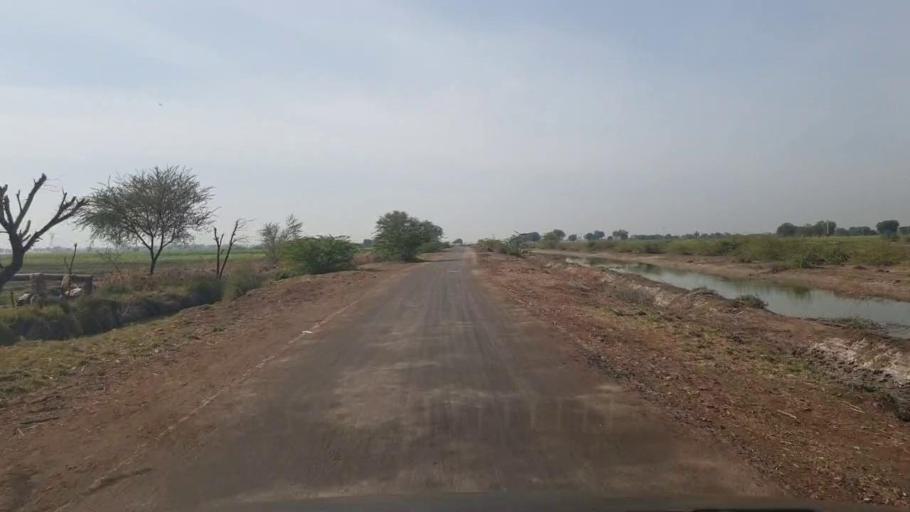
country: PK
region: Sindh
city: Umarkot
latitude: 25.3609
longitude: 69.6818
